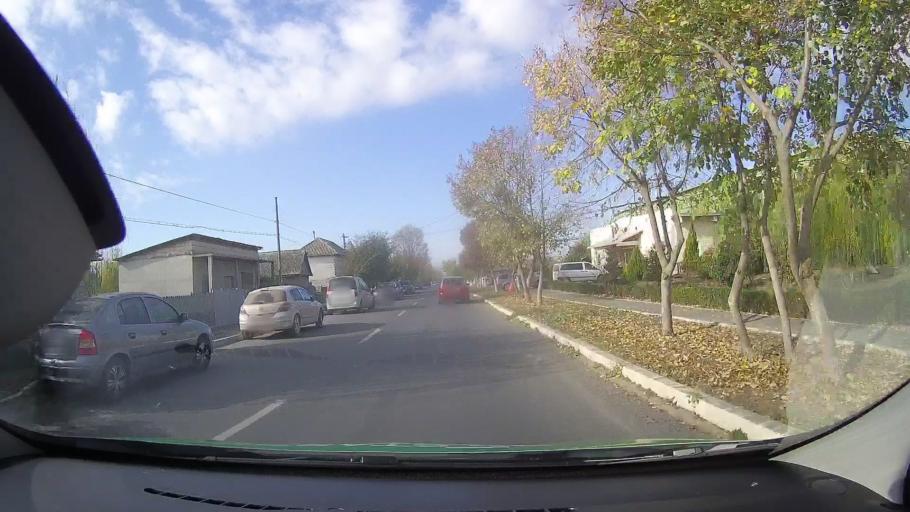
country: RO
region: Tulcea
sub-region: Comuna Sarichioi
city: Sarichioi
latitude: 44.9433
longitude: 28.8495
